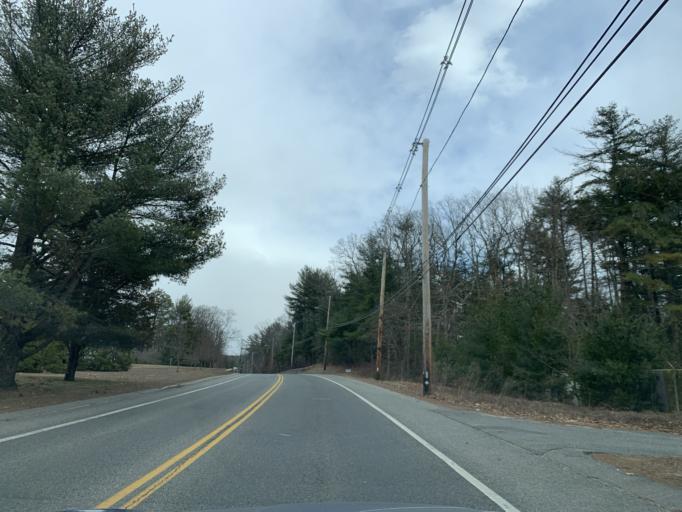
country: US
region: Rhode Island
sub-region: Providence County
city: Woonsocket
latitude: 42.0357
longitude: -71.4765
